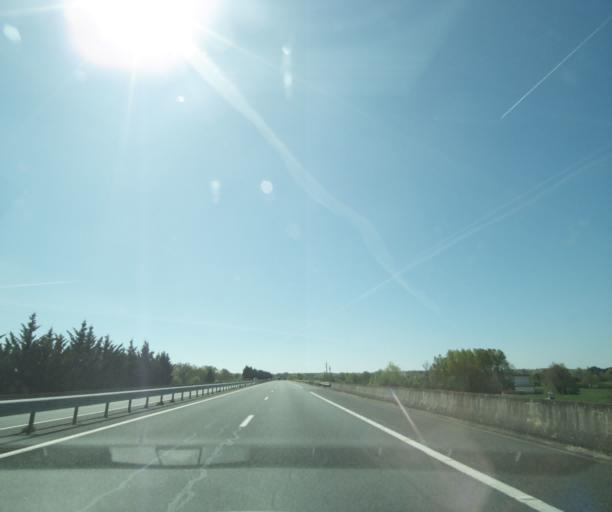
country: FR
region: Centre
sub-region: Departement de l'Indre
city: Le Pechereau
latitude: 46.5257
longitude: 1.5148
